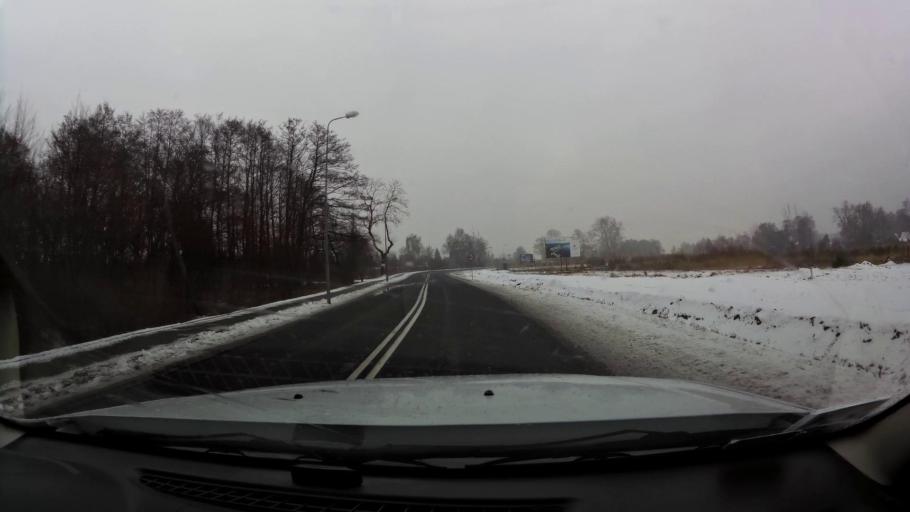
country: PL
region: West Pomeranian Voivodeship
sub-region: Powiat gryficki
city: Mrzezyno
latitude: 54.1381
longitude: 15.2858
